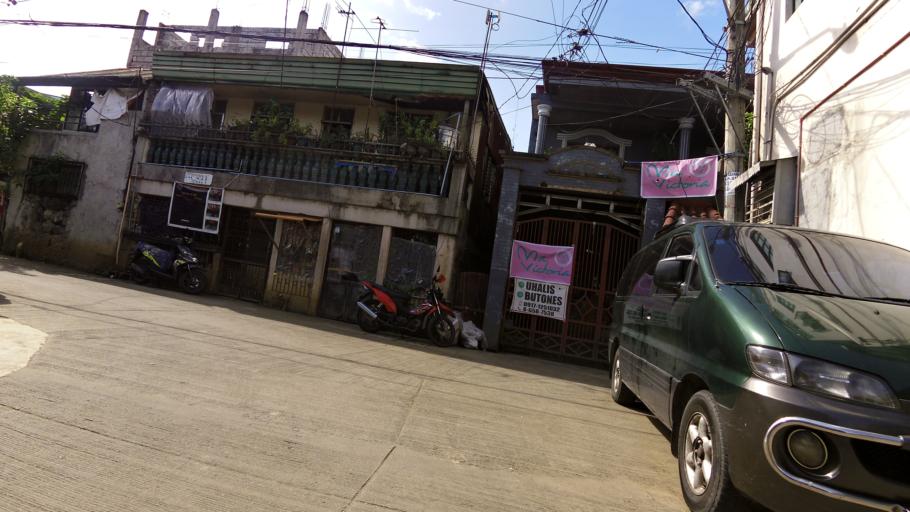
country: PH
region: Calabarzon
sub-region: Province of Rizal
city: Taytay
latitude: 14.5681
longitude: 121.1293
